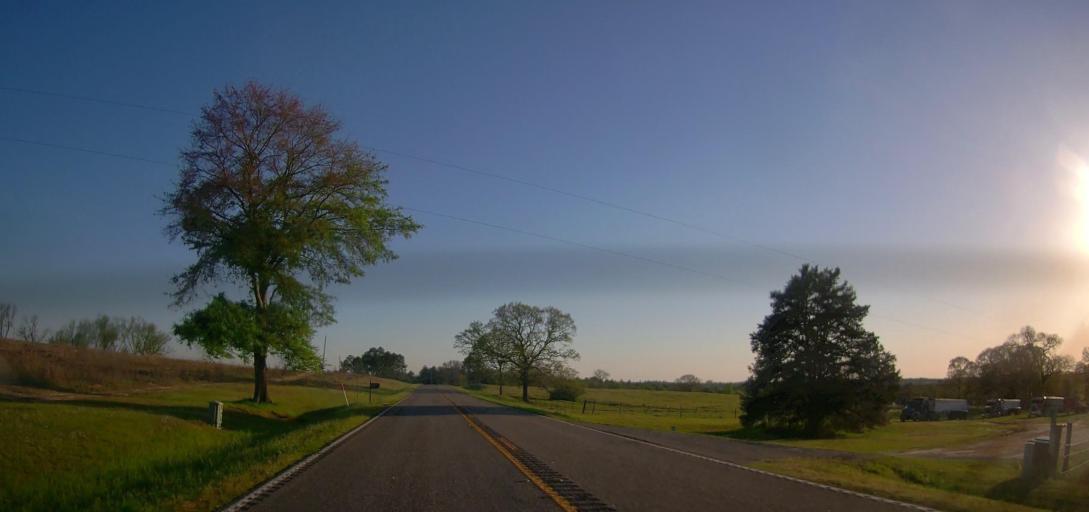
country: US
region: Georgia
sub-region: Marion County
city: Buena Vista
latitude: 32.4028
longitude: -84.4406
